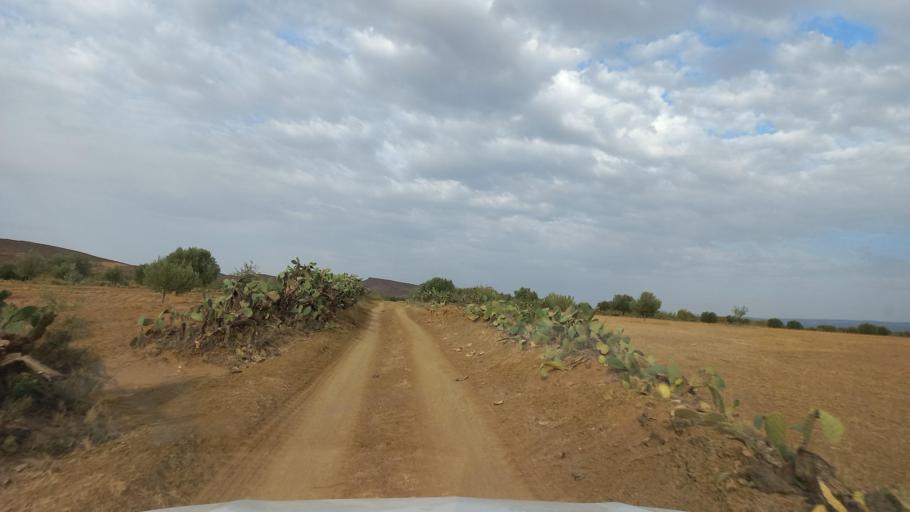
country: TN
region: Al Qasrayn
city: Kasserine
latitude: 35.1881
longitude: 9.0515
